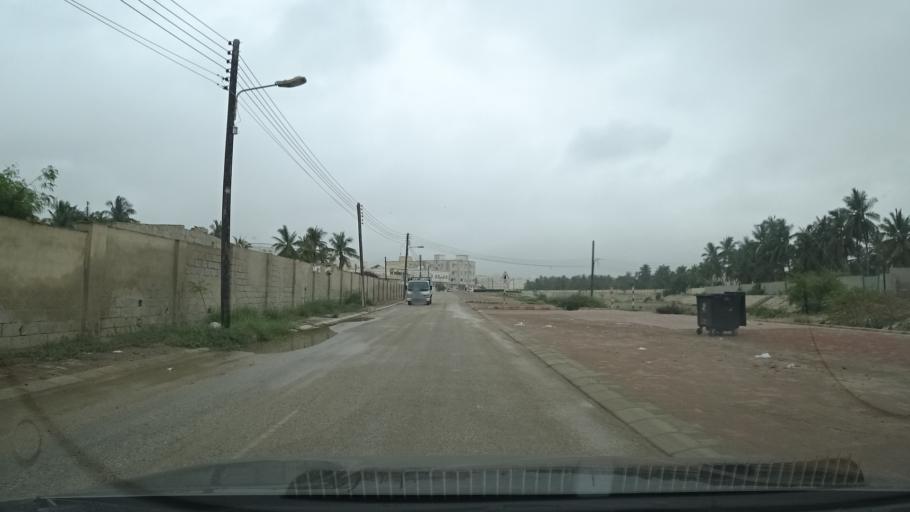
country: OM
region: Zufar
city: Salalah
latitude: 17.0100
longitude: 54.0640
